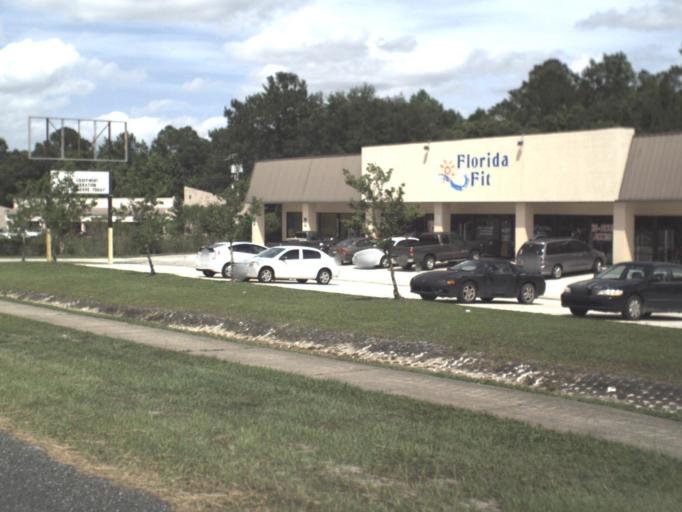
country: US
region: Florida
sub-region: Clay County
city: Middleburg
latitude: 30.0581
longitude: -81.8798
